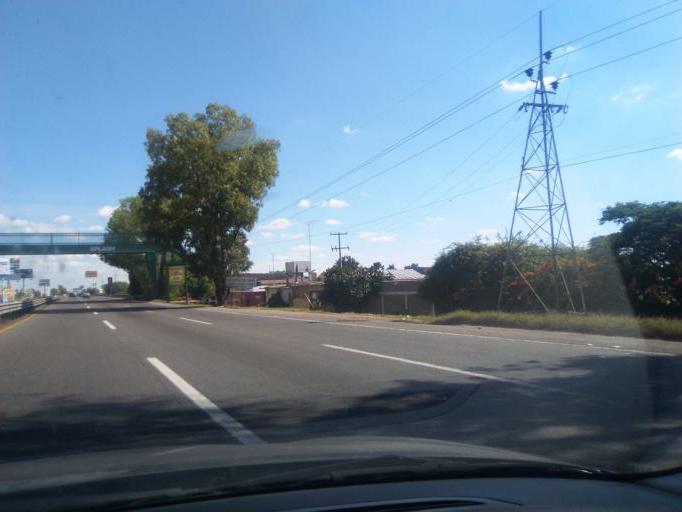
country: MX
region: Guanajuato
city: Colonia Nuevo Mexico
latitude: 20.9751
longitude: -101.4706
